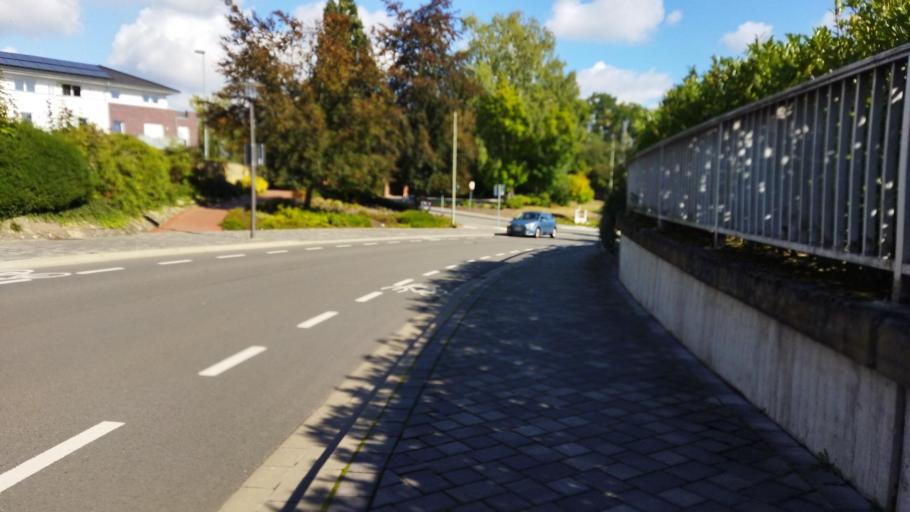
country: DE
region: Lower Saxony
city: Salzbergen
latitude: 52.3241
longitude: 7.3472
